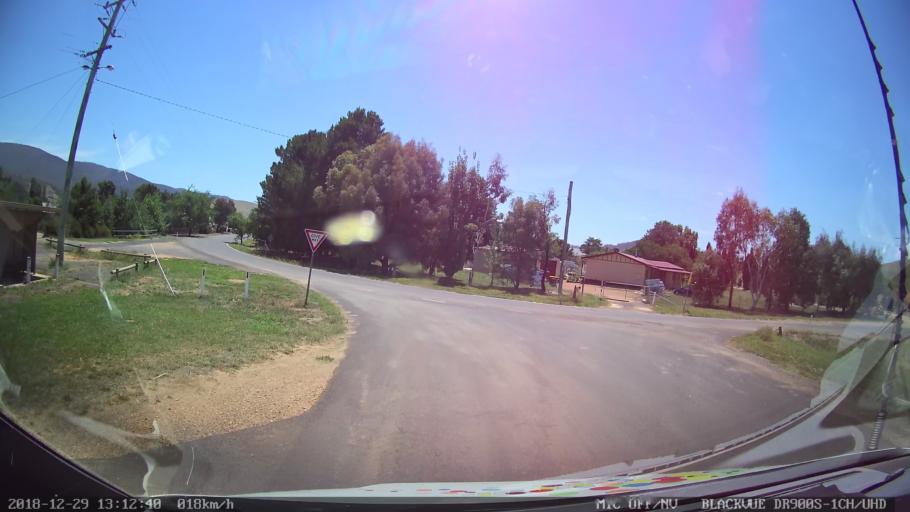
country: AU
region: Australian Capital Territory
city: Macarthur
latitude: -35.7097
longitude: 149.1654
